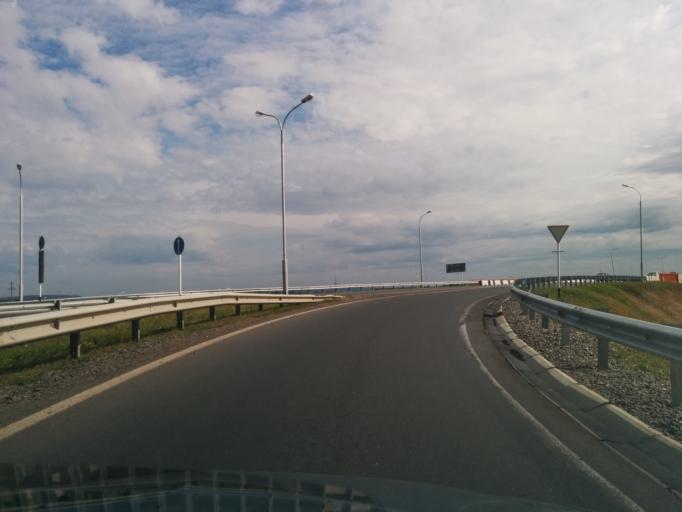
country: RU
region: Bashkortostan
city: Kabakovo
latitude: 54.4924
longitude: 55.9042
